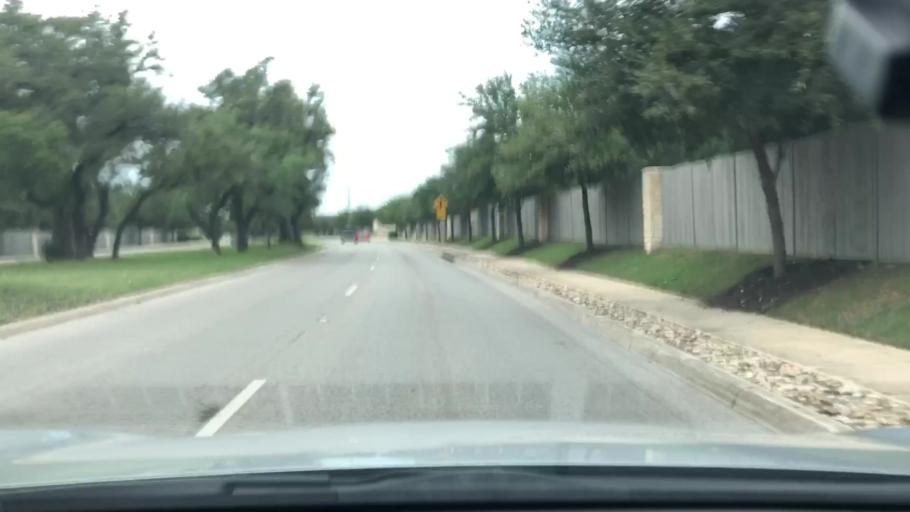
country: US
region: Texas
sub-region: Bexar County
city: Leon Valley
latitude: 29.4553
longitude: -98.6687
